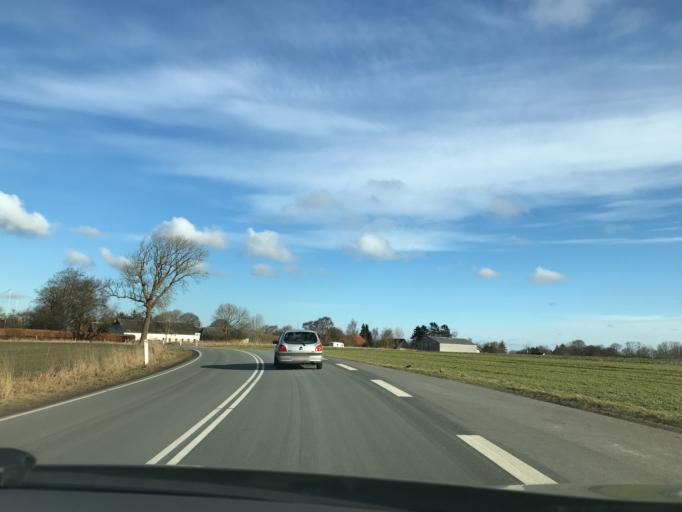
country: DK
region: South Denmark
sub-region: Nordfyns Kommune
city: Bogense
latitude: 55.5226
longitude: 10.0746
